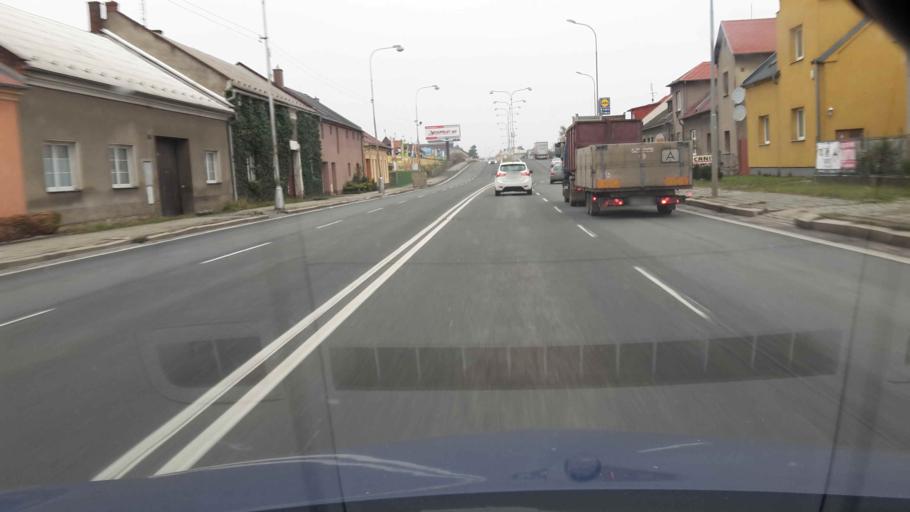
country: CZ
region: Olomoucky
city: Grygov
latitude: 49.5783
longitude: 17.2952
